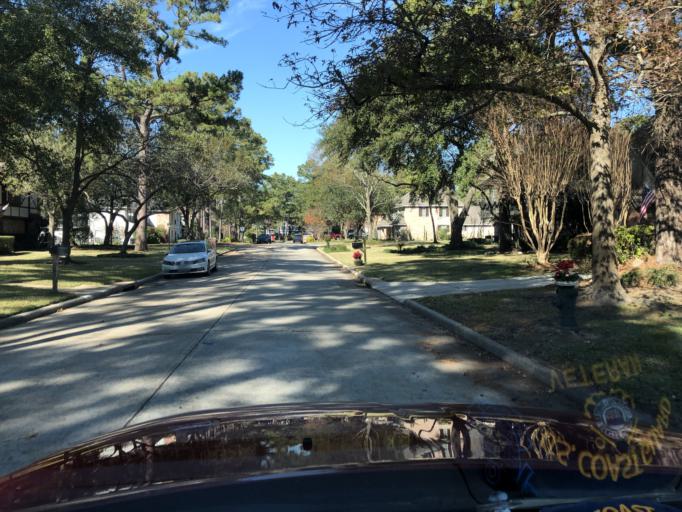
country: US
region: Texas
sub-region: Harris County
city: Tomball
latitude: 30.0234
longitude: -95.5504
